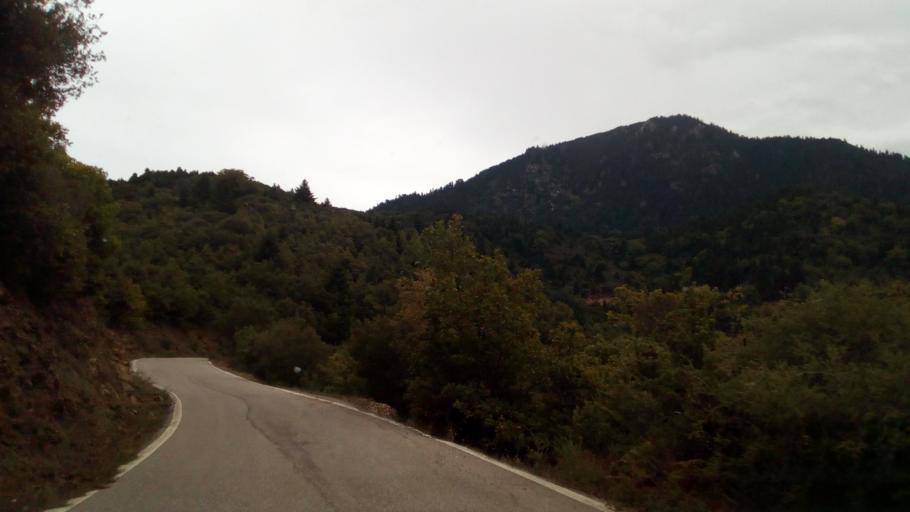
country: GR
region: West Greece
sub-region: Nomos Aitolias kai Akarnanias
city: Thermo
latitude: 38.5871
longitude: 21.8455
